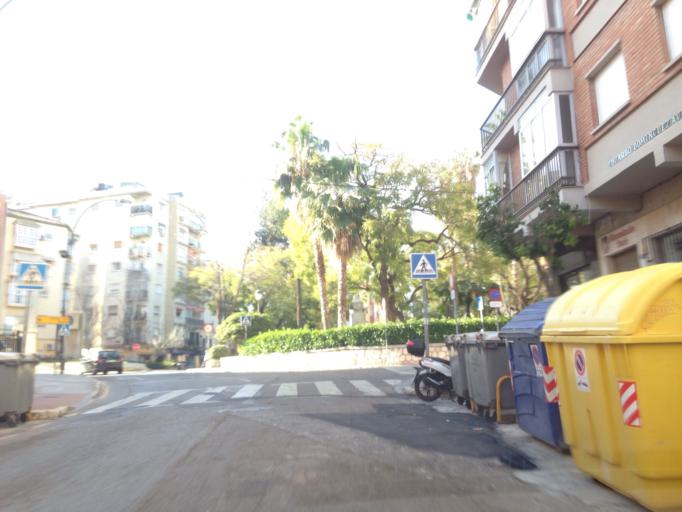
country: ES
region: Andalusia
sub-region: Provincia de Malaga
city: Malaga
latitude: 36.7297
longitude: -4.4213
